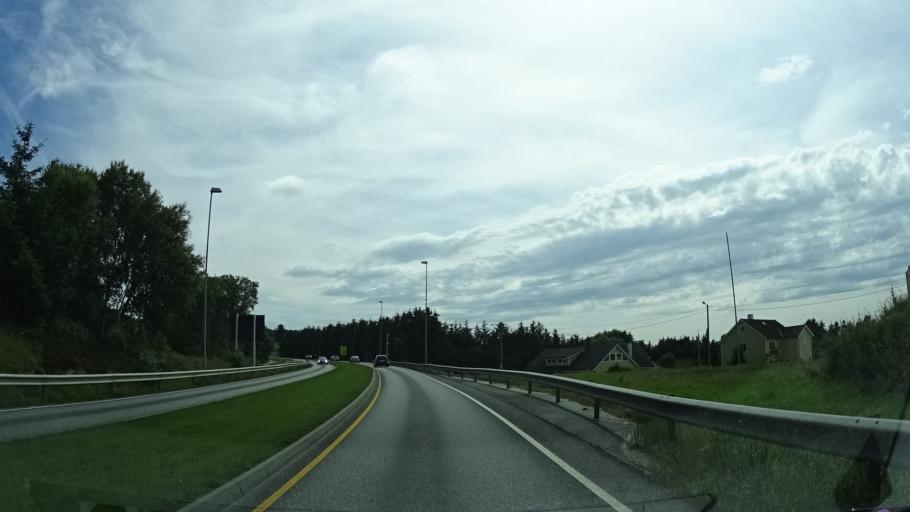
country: NO
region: Rogaland
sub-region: Randaberg
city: Randaberg
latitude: 58.9917
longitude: 5.6533
